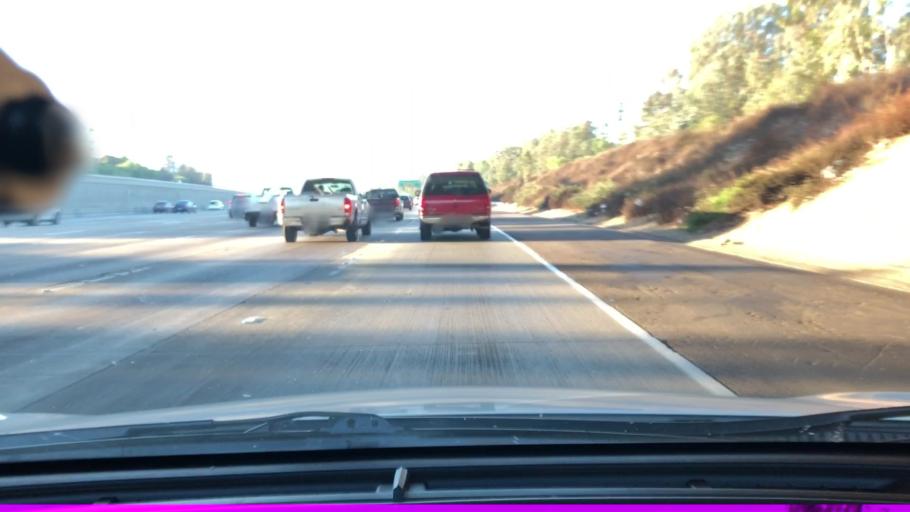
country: US
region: California
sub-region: San Diego County
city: Poway
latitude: 33.0330
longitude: -117.0782
